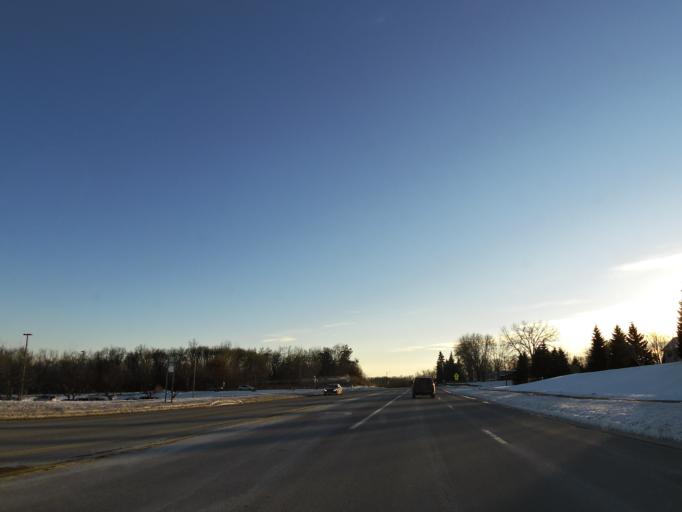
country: US
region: Minnesota
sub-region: Hennepin County
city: Shorewood
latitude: 44.8616
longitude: -93.5803
